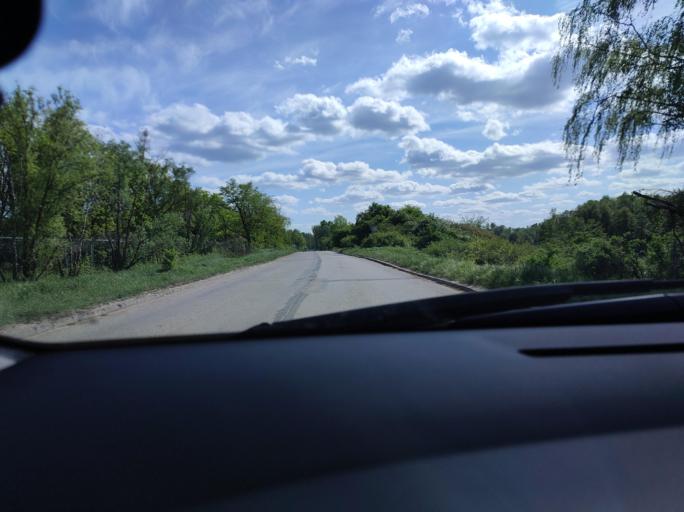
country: PL
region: West Pomeranian Voivodeship
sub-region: Powiat policki
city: Police
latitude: 53.5756
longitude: 14.5281
